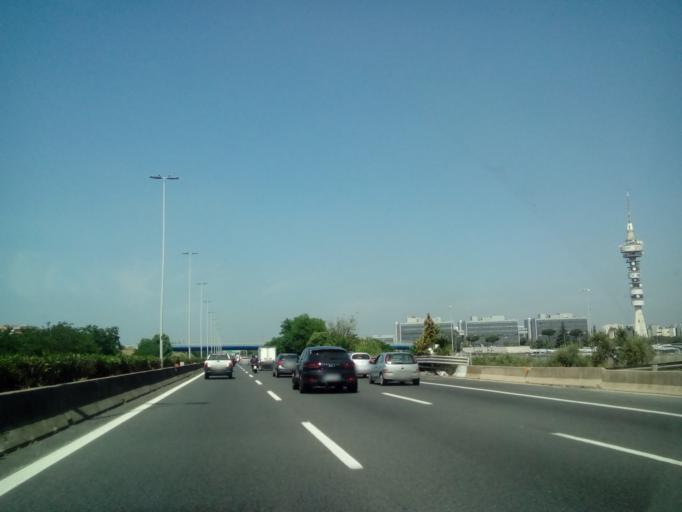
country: IT
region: Latium
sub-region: Citta metropolitana di Roma Capitale
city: Selcetta
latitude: 41.7959
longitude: 12.4951
